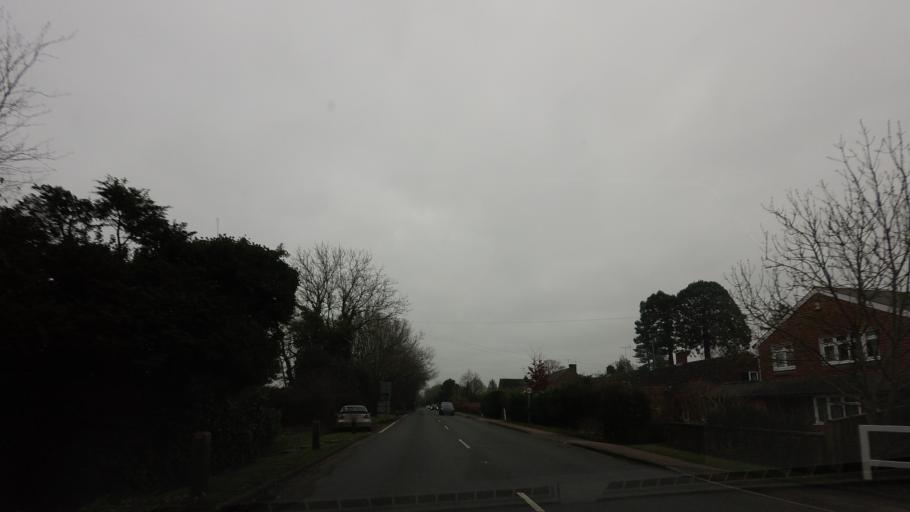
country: GB
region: England
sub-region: Kent
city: Cranbrook
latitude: 51.1094
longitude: 0.5472
